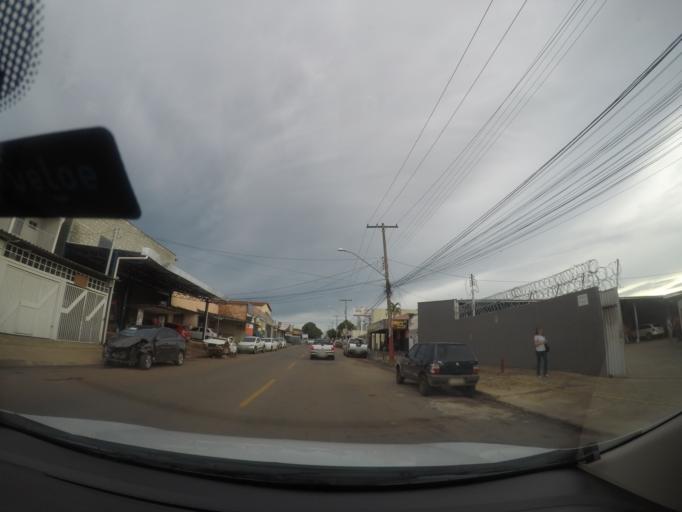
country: BR
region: Goias
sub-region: Goiania
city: Goiania
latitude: -16.6969
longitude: -49.3078
